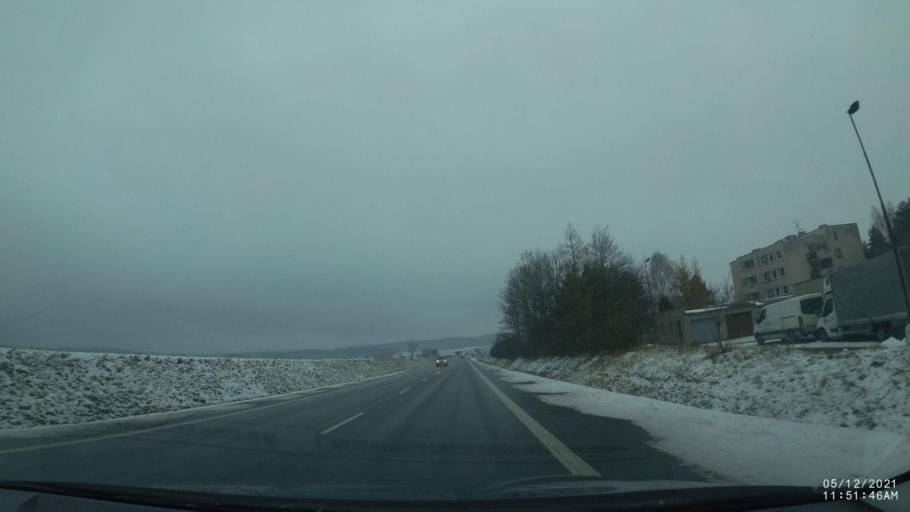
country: CZ
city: Dobruska
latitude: 50.2918
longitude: 16.1694
